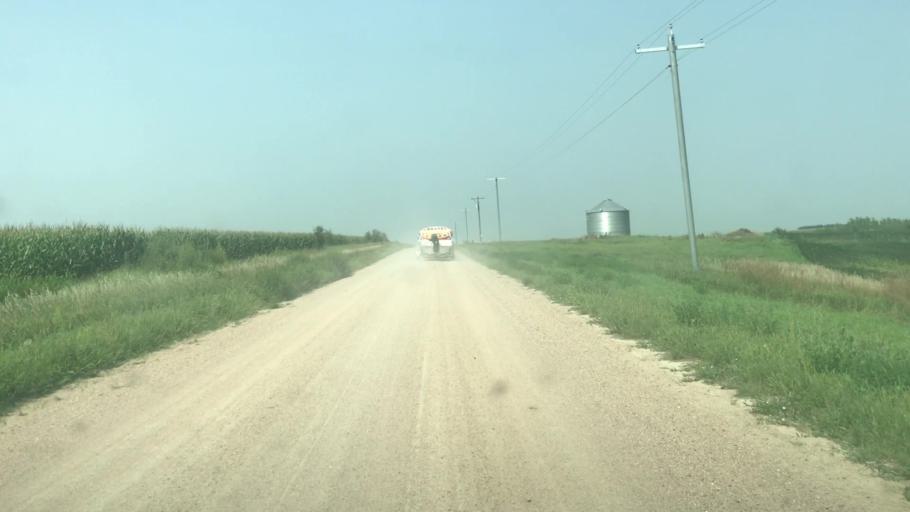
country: US
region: Nebraska
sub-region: Sherman County
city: Loup City
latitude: 41.2685
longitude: -98.9191
